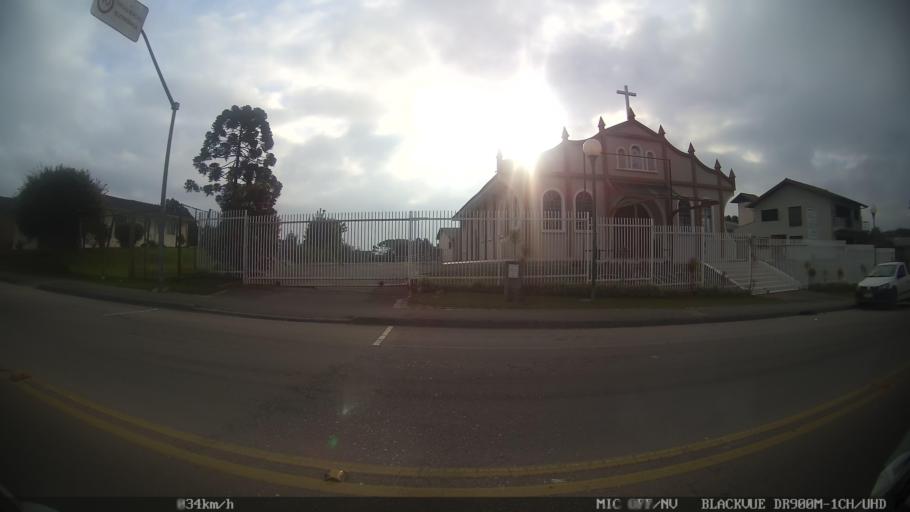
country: BR
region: Parana
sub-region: Curitiba
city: Curitiba
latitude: -25.4010
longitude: -49.3122
